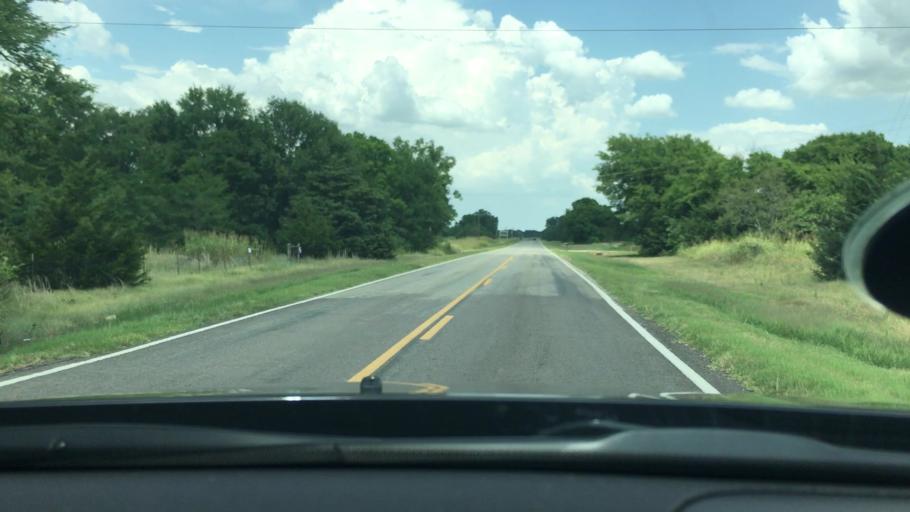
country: US
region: Oklahoma
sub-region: Marshall County
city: Oakland
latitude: 34.0085
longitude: -96.8795
